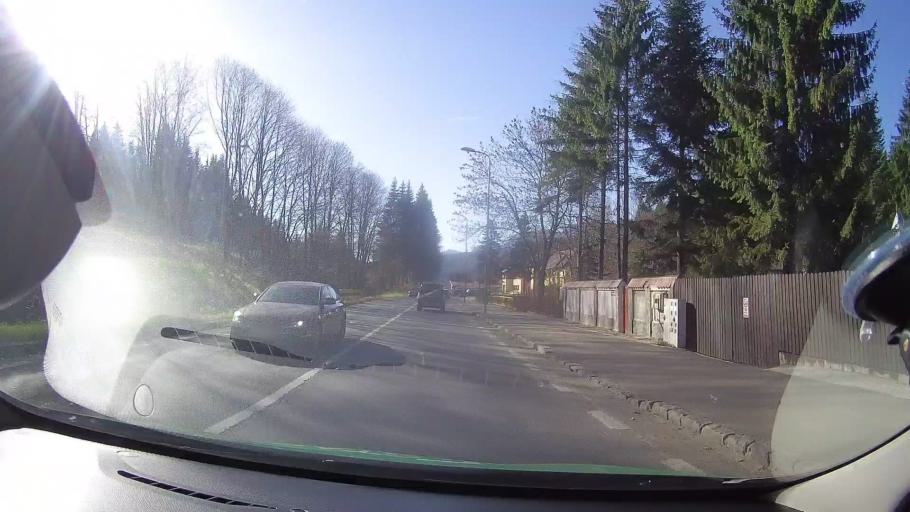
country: RO
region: Brasov
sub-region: Oras Predeal
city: Predeal
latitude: 45.4986
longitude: 25.5732
